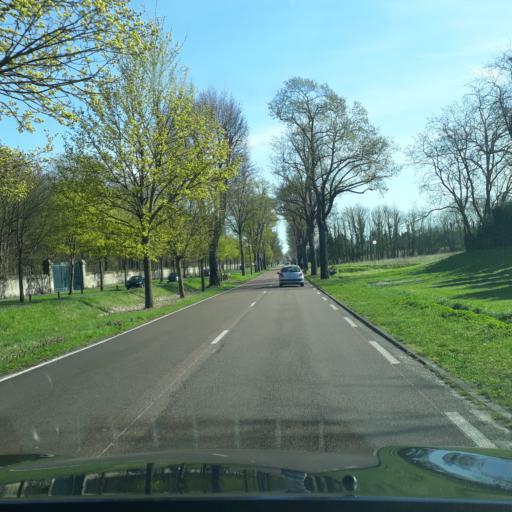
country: FR
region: Ile-de-France
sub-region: Departement de l'Essonne
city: Mennecy
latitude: 48.5591
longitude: 2.4241
